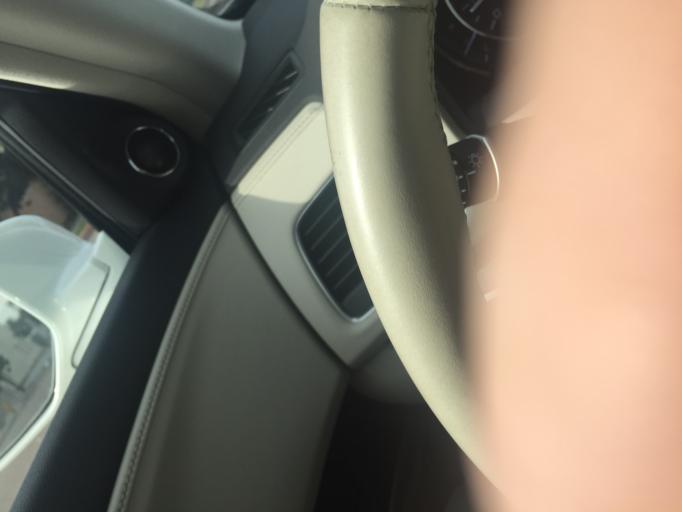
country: US
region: California
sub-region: San Diego County
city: San Diego
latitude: 32.7571
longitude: -117.1021
